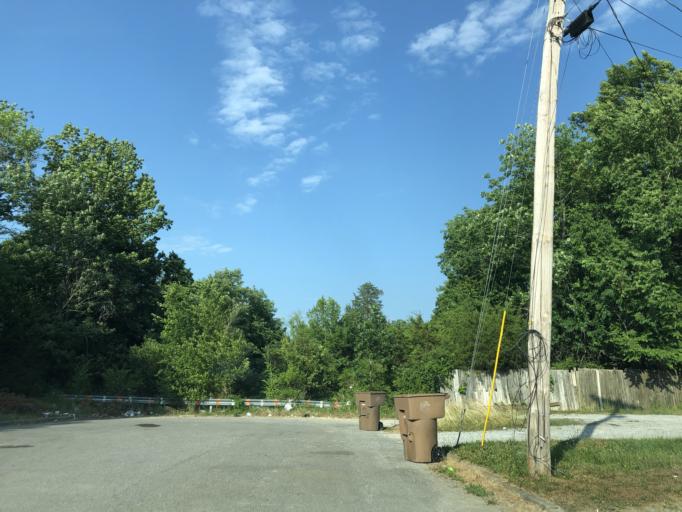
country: US
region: Tennessee
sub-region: Davidson County
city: Nashville
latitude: 36.2230
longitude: -86.8007
